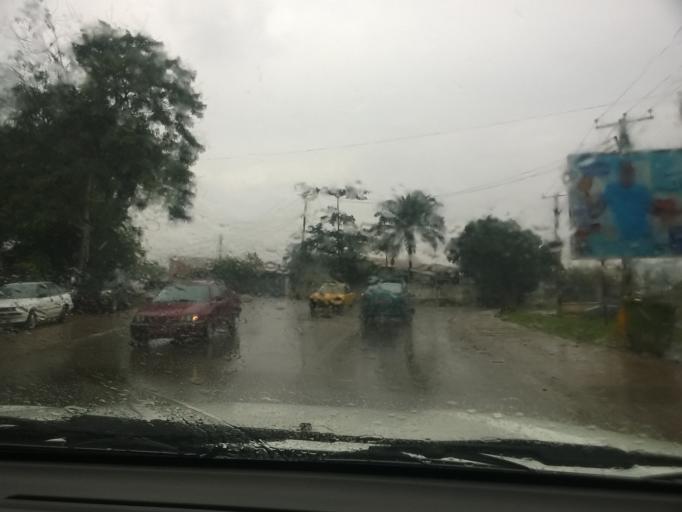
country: CM
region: Centre
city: Yaounde
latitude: 3.8786
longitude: 11.5170
